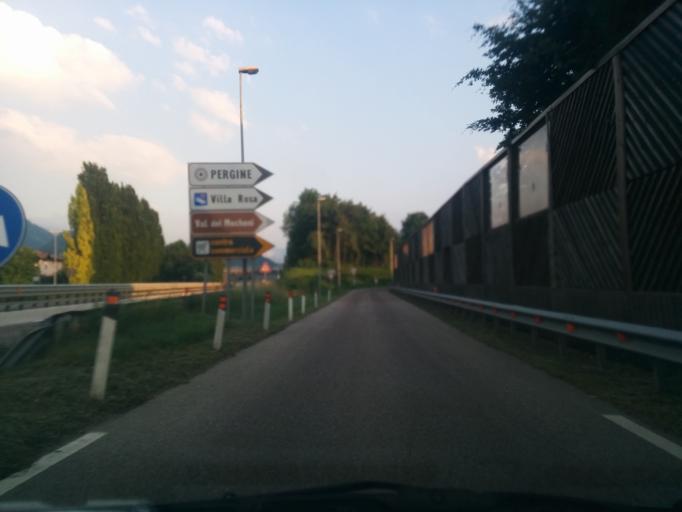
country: IT
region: Trentino-Alto Adige
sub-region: Provincia di Trento
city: Pergine Valsugana
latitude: 46.0625
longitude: 11.2275
